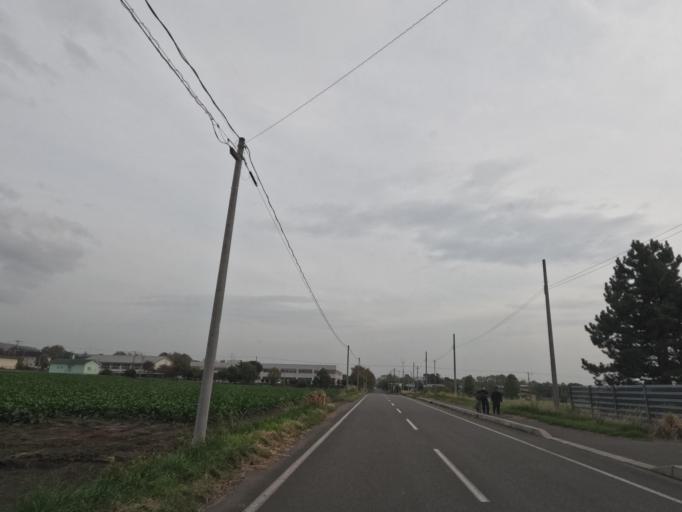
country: JP
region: Hokkaido
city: Date
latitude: 42.4304
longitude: 140.9072
